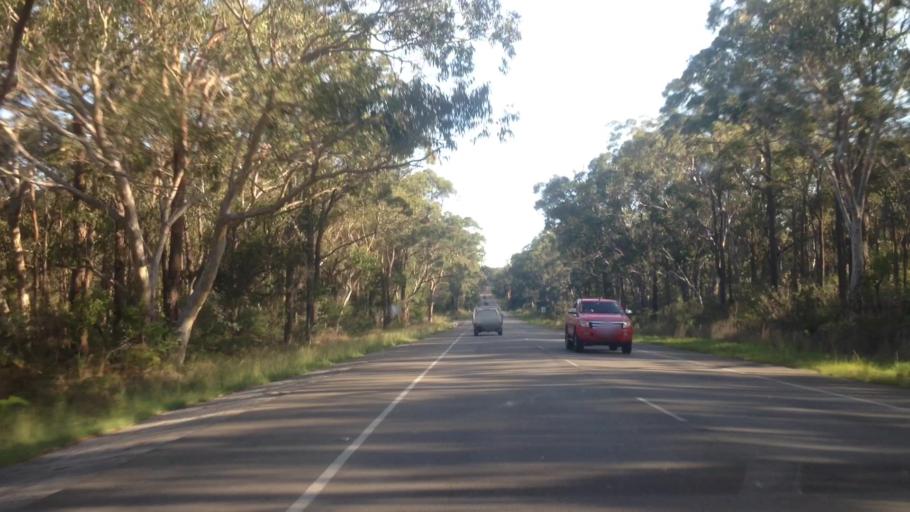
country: AU
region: New South Wales
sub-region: Lake Macquarie Shire
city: Dora Creek
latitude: -33.1322
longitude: 151.4768
